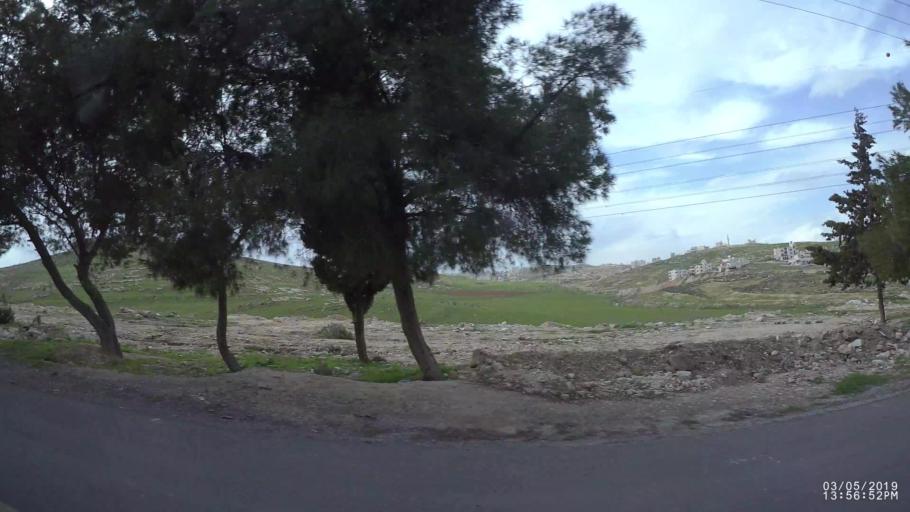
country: JO
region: Amman
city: Amman
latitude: 32.0166
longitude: 35.9354
